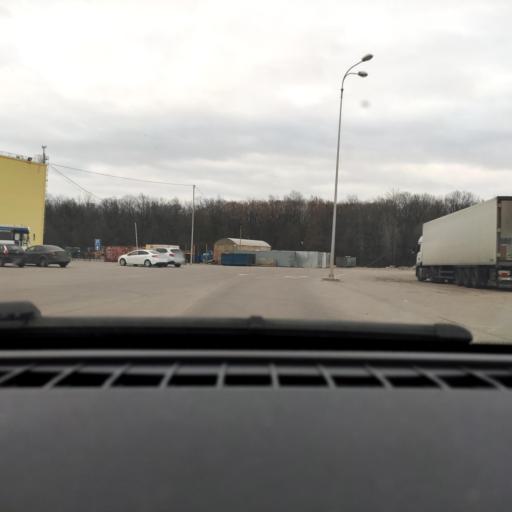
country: RU
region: Voronezj
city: Podgornoye
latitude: 51.7855
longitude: 39.2030
